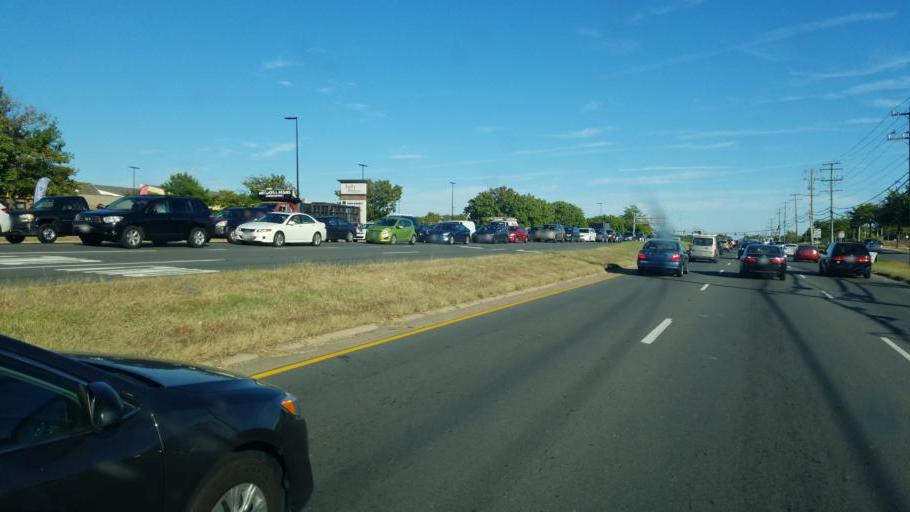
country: US
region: Virginia
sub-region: Fairfax County
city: Chantilly
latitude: 38.8936
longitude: -77.4301
